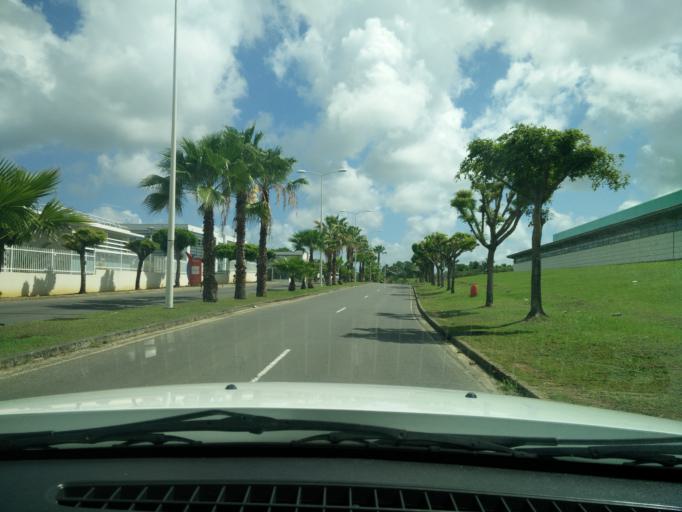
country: GP
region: Guadeloupe
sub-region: Guadeloupe
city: Les Abymes
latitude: 16.2683
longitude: -61.5178
